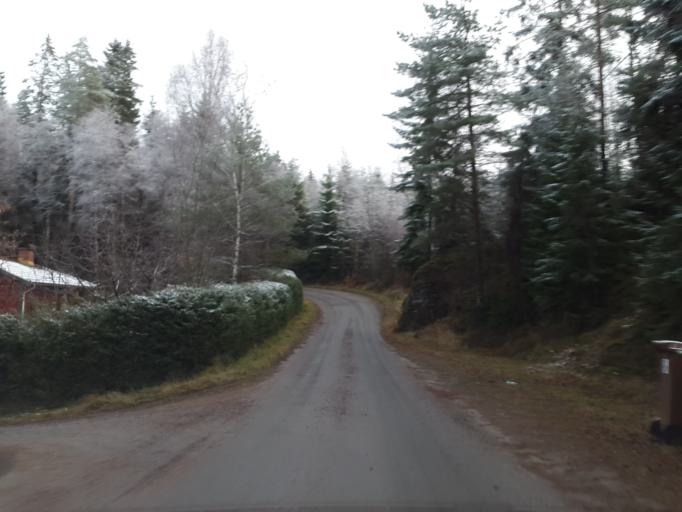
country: SE
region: Vaestra Goetaland
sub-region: Vargarda Kommun
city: Jonstorp
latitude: 57.8465
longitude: 12.6813
